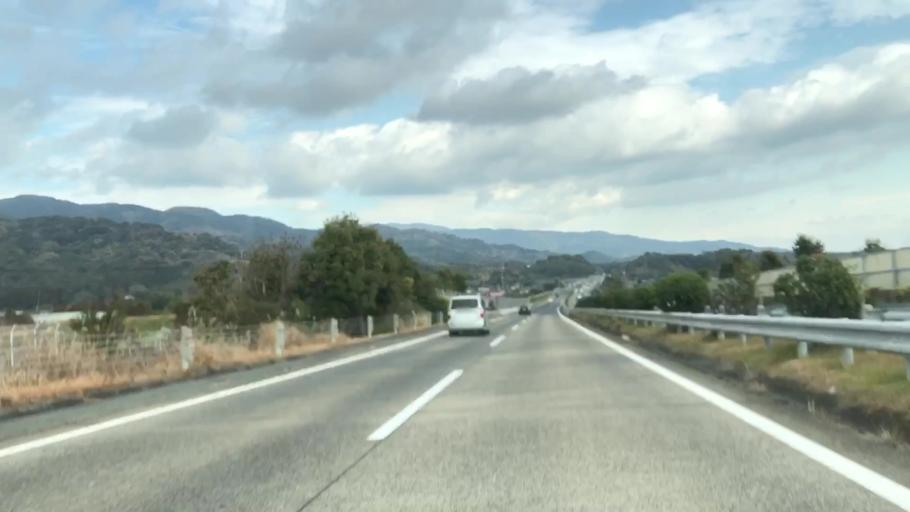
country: JP
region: Saga Prefecture
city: Kanzakimachi-kanzaki
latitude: 33.3443
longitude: 130.3619
